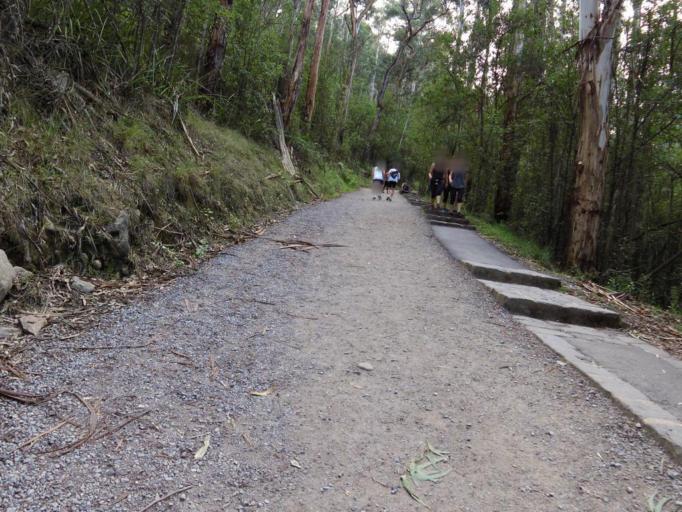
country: AU
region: Victoria
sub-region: Yarra Ranges
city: Ferny Creek
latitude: -37.8838
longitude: 145.3165
